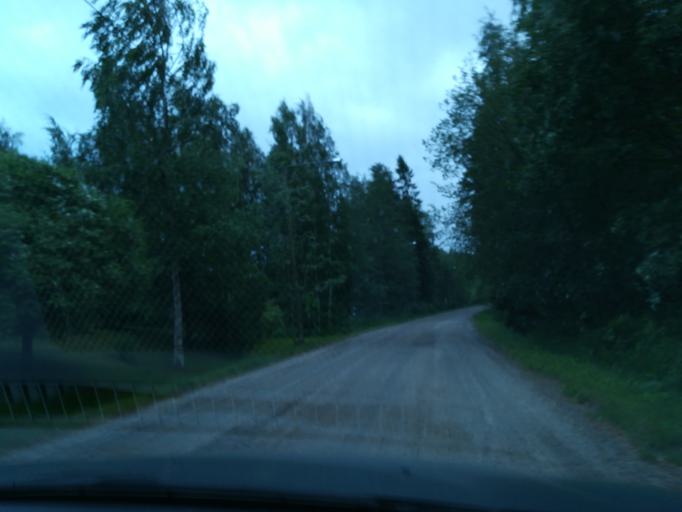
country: FI
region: Southern Savonia
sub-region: Mikkeli
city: Ristiina
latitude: 61.4928
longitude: 27.2783
